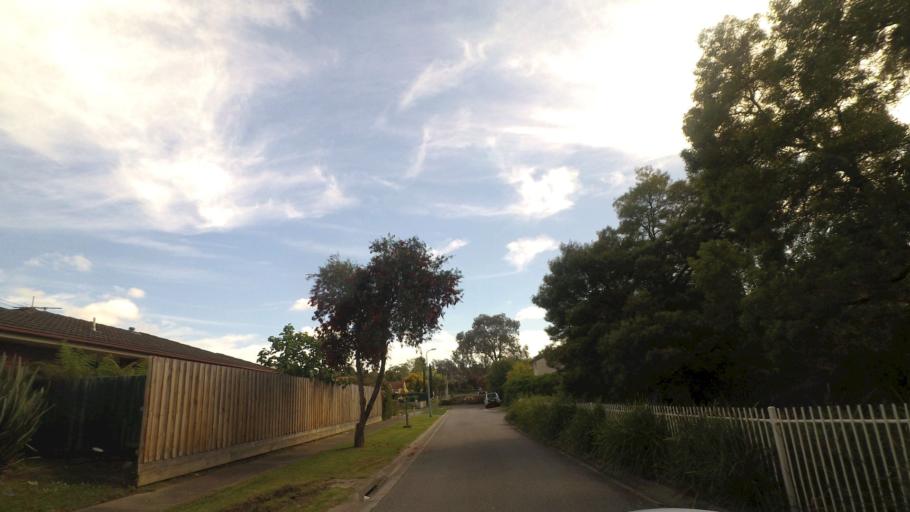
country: AU
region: Victoria
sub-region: Knox
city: Bayswater
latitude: -37.8514
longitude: 145.2587
